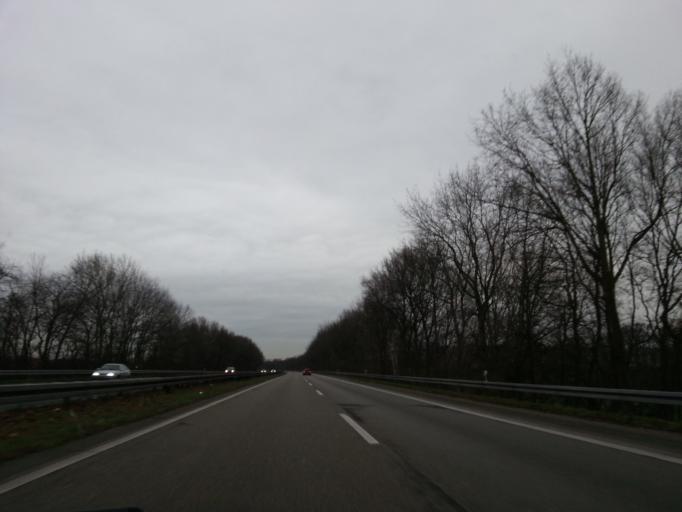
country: DE
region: North Rhine-Westphalia
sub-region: Regierungsbezirk Dusseldorf
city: Wesel
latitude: 51.6950
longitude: 6.6704
